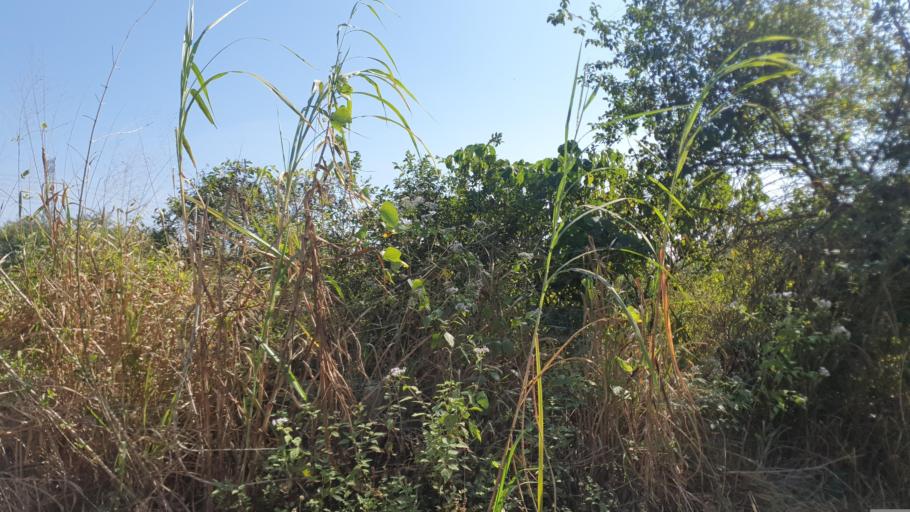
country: TW
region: Taiwan
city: Yujing
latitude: 23.0482
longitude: 120.3733
